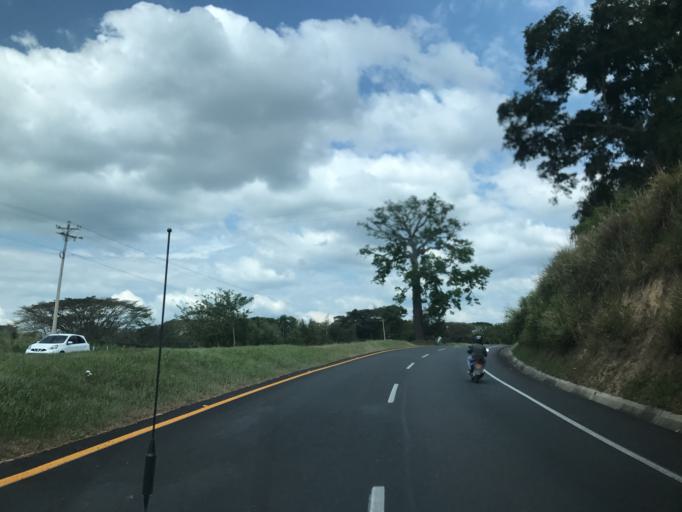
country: CO
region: Valle del Cauca
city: Obando
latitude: 4.6098
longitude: -75.9549
